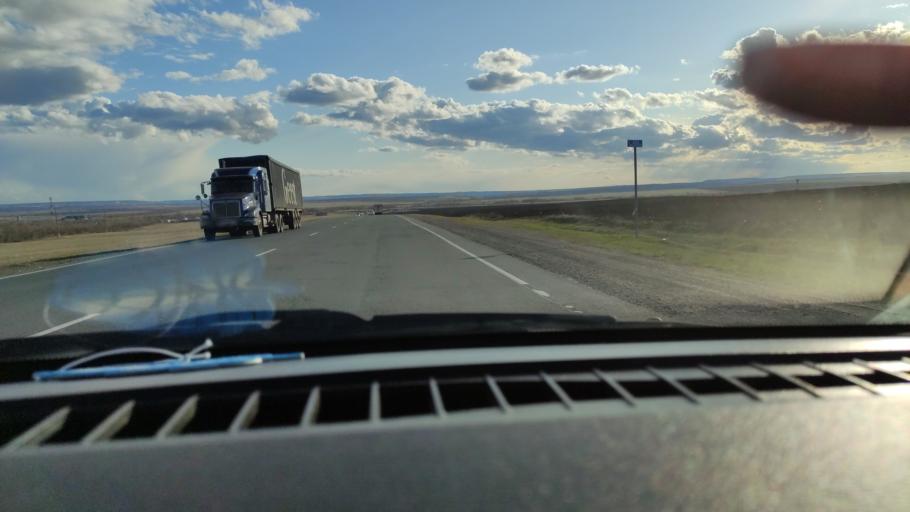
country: RU
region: Saratov
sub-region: Saratovskiy Rayon
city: Saratov
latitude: 51.7413
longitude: 46.0454
